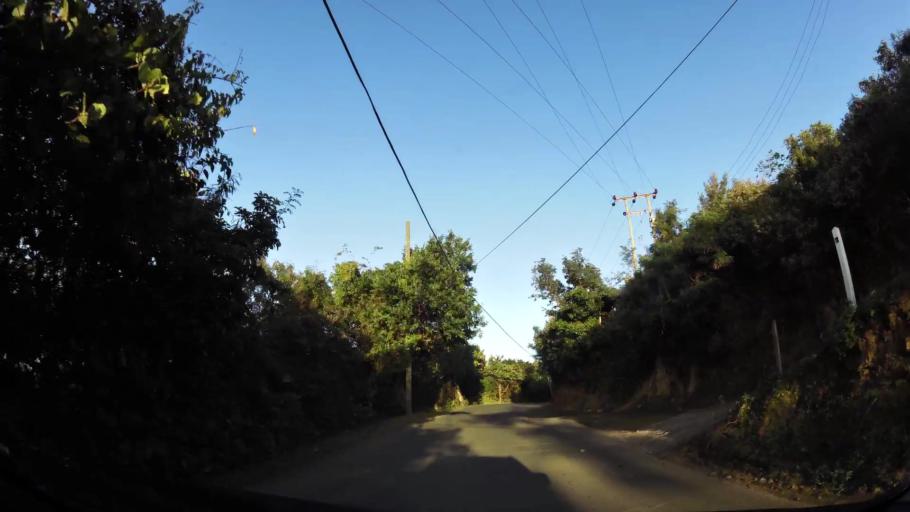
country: VG
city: Road Town
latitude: 18.4387
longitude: -64.6203
